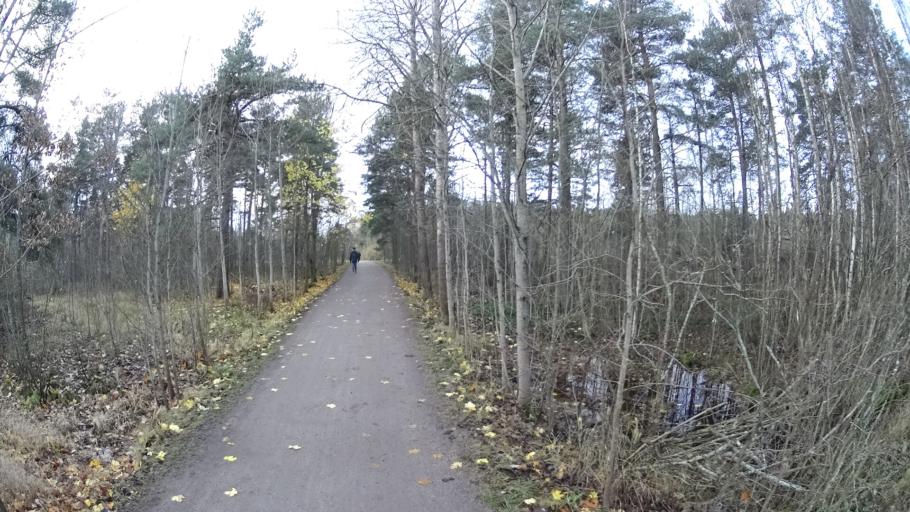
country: FI
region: Uusimaa
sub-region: Helsinki
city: Helsinki
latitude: 60.1940
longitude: 24.9149
